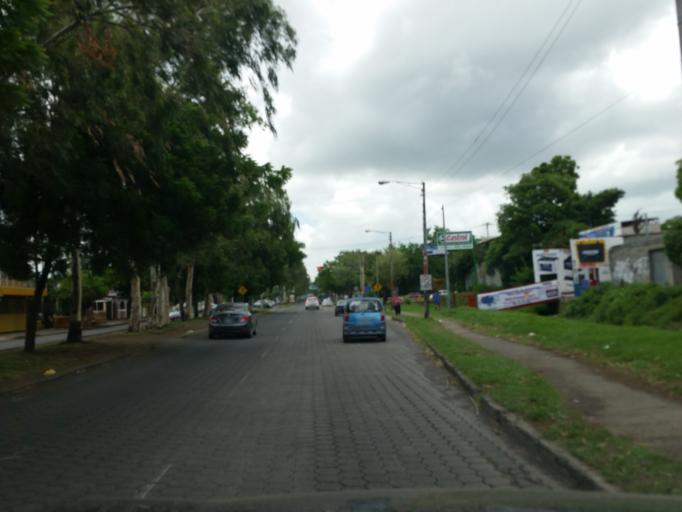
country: NI
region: Managua
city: Managua
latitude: 12.1288
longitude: -86.2448
